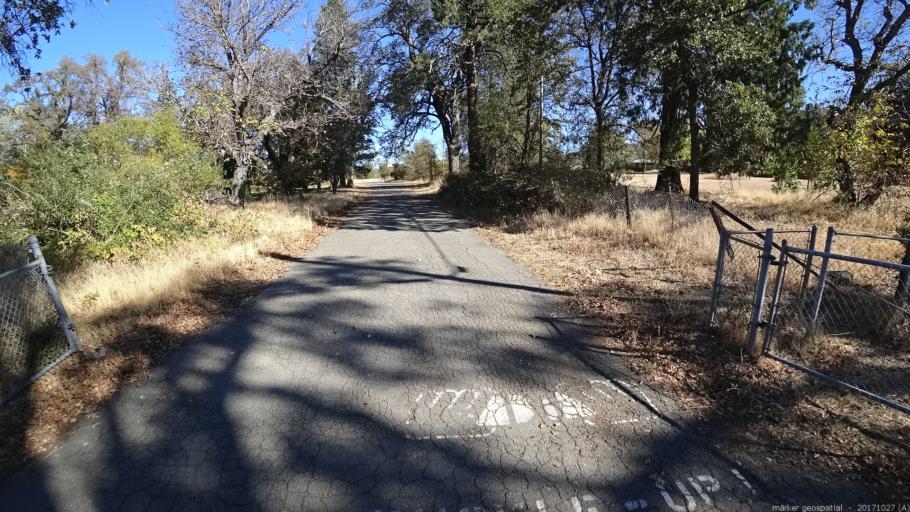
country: US
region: California
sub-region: Shasta County
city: Burney
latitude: 40.7933
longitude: -121.9407
